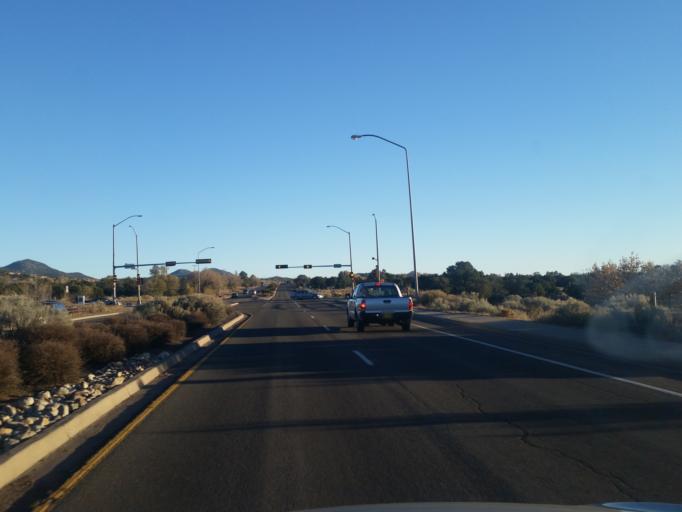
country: US
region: New Mexico
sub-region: Santa Fe County
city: Santa Fe
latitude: 35.6521
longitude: -105.9369
